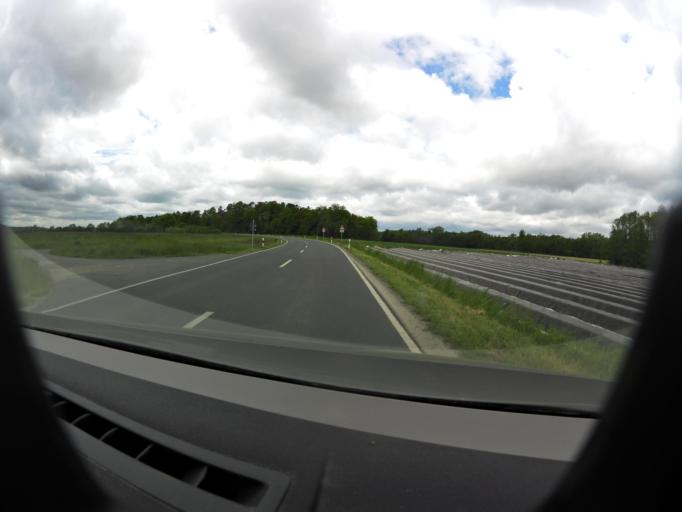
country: DE
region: Bavaria
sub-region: Regierungsbezirk Unterfranken
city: Wiesentheid
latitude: 49.7932
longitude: 10.3249
